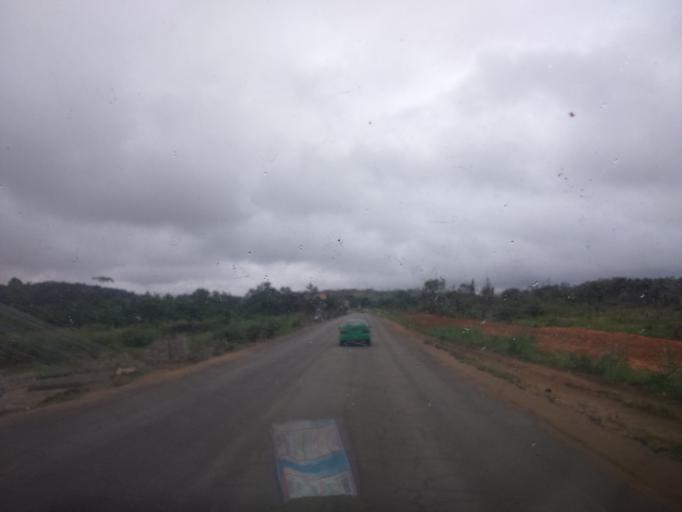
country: CI
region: Sud-Comoe
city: Bonoua
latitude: 5.2477
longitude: -3.6218
